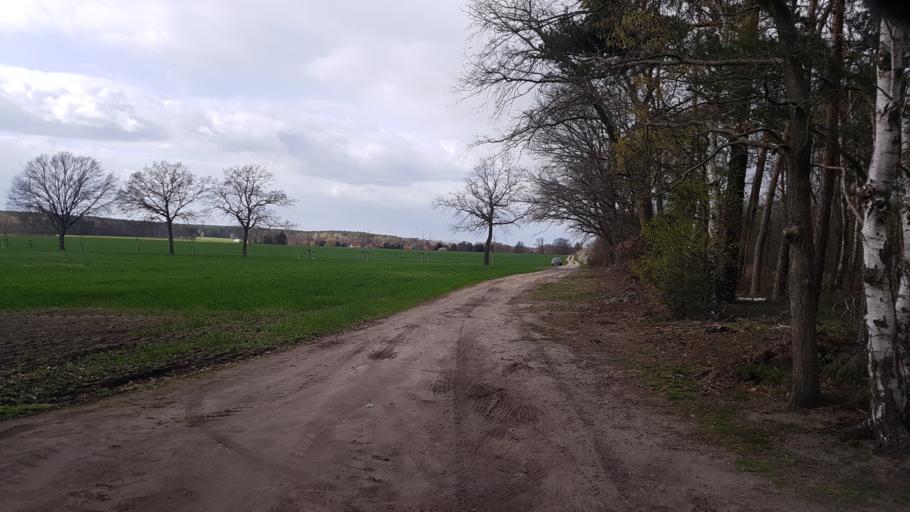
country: DE
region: Brandenburg
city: Calau
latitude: 51.7374
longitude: 13.9277
